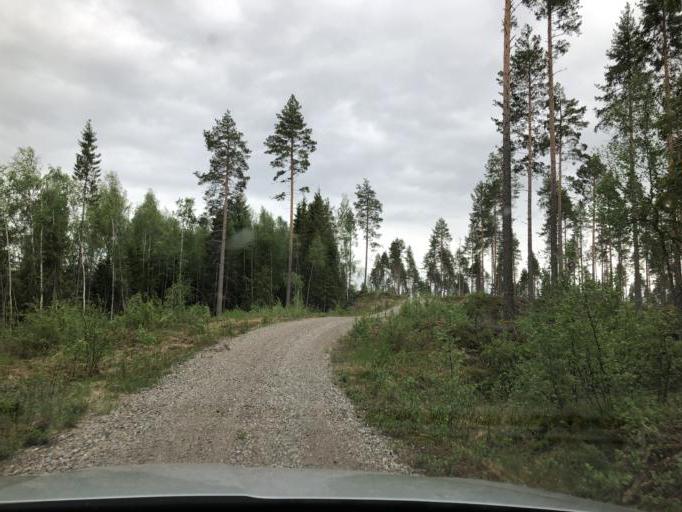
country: SE
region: Norrbotten
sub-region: Pitea Kommun
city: Roknas
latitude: 65.4003
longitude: 21.2684
